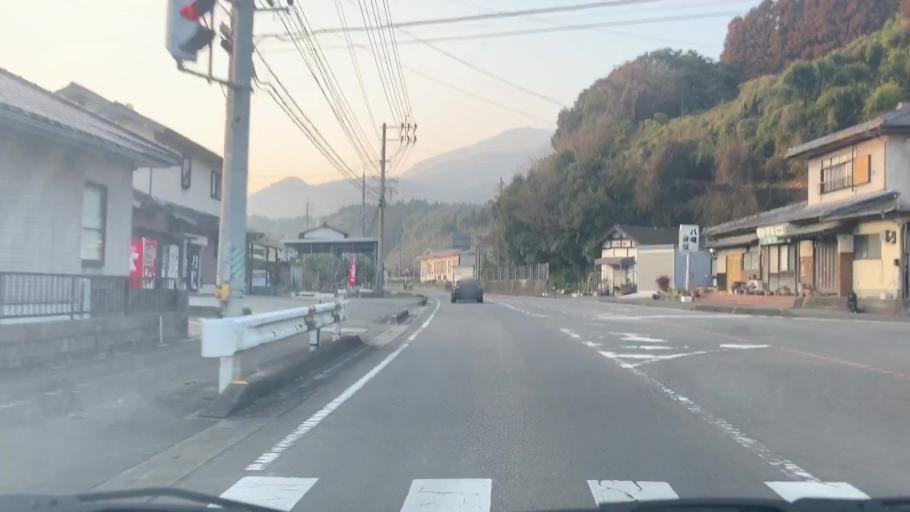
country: JP
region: Saga Prefecture
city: Takeocho-takeo
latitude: 33.2629
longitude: 130.0571
